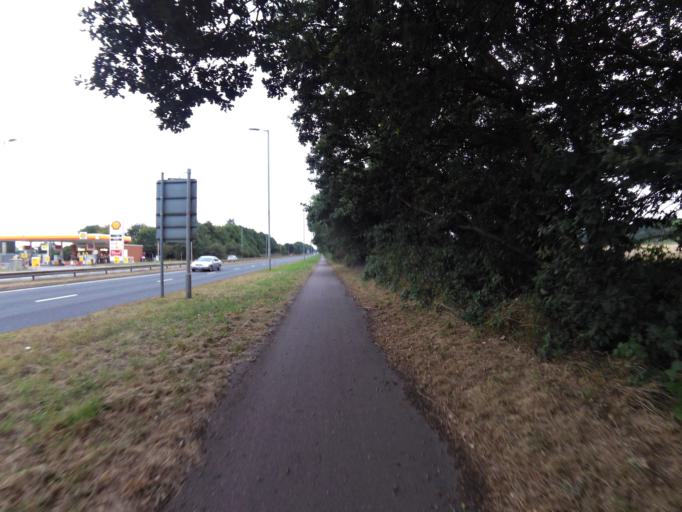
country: GB
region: England
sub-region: Hertfordshire
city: Shenley AV
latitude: 51.7384
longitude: -0.2784
